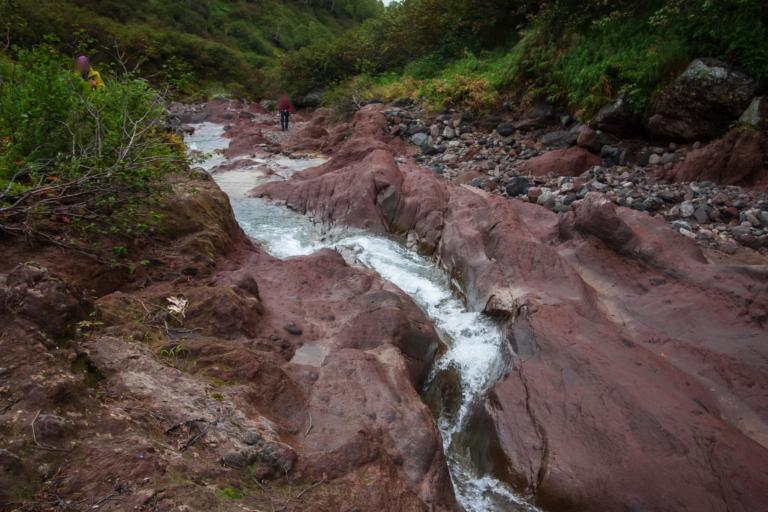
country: RU
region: Kamtsjatka
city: Petropavlovsk-Kamchatsky
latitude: 53.5893
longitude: 158.9156
